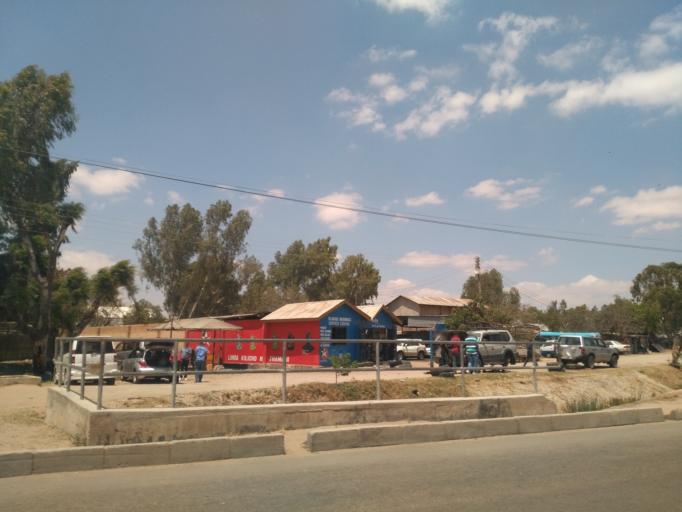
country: TZ
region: Dodoma
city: Dodoma
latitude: -6.1747
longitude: 35.7545
